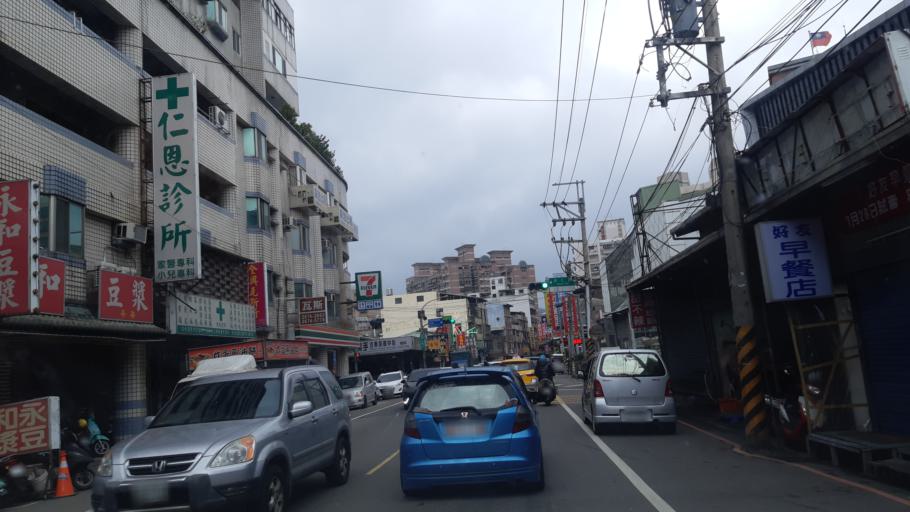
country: TW
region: Taiwan
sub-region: Taoyuan
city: Taoyuan
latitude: 24.9370
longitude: 121.3634
